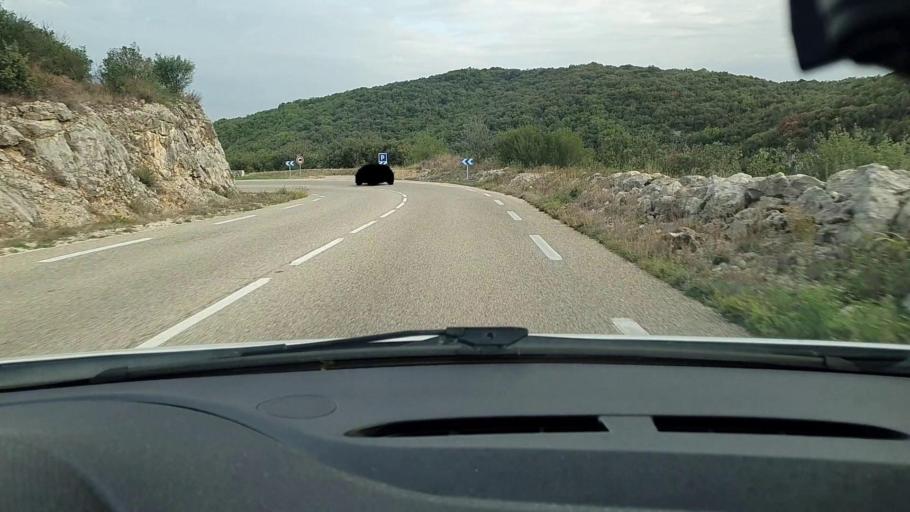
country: FR
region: Languedoc-Roussillon
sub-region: Departement du Gard
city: Barjac
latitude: 44.2288
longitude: 4.3183
